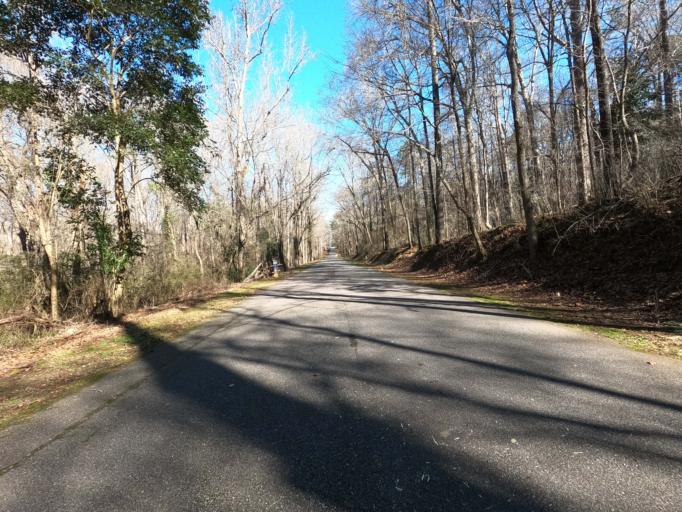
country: US
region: Georgia
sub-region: Clarke County
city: Athens
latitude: 33.9839
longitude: -83.3830
